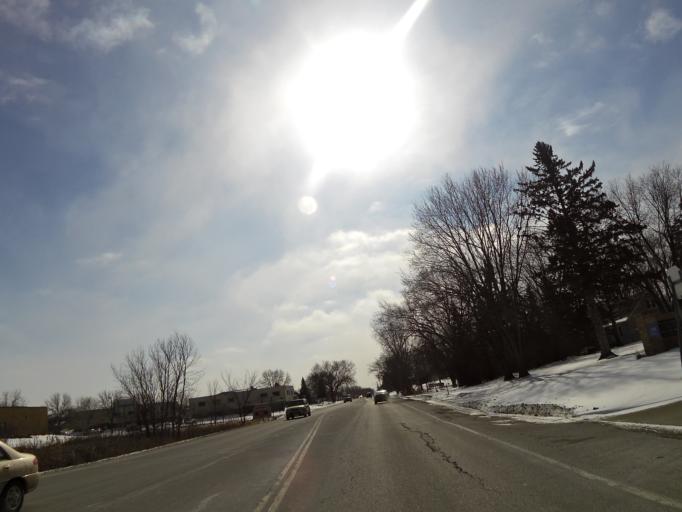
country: US
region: Minnesota
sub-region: Ramsey County
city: Maplewood
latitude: 44.9697
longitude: -92.9850
